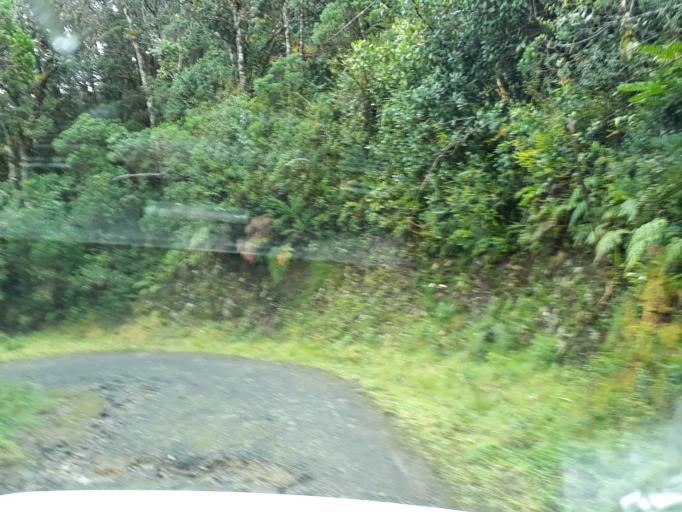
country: CO
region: Cundinamarca
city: Junin
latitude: 4.7123
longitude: -73.6280
